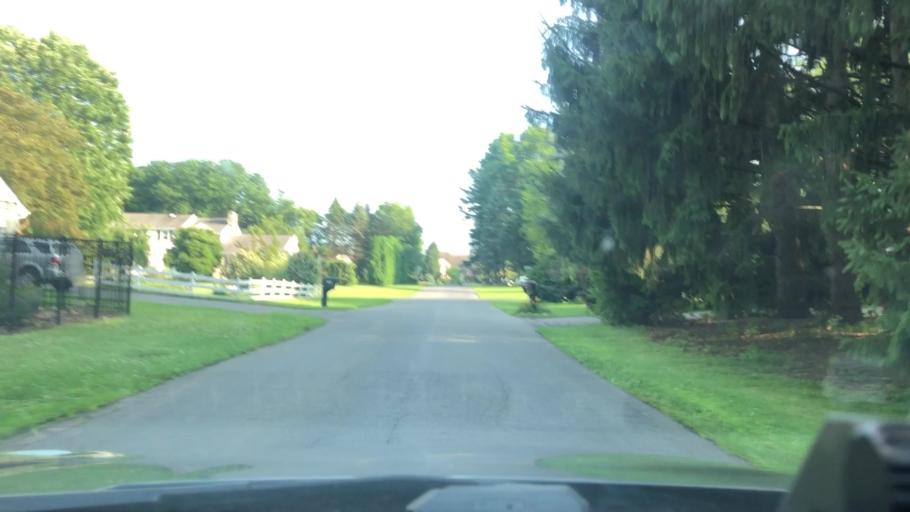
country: US
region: Pennsylvania
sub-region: Northampton County
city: Bethlehem
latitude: 40.6549
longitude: -75.3920
